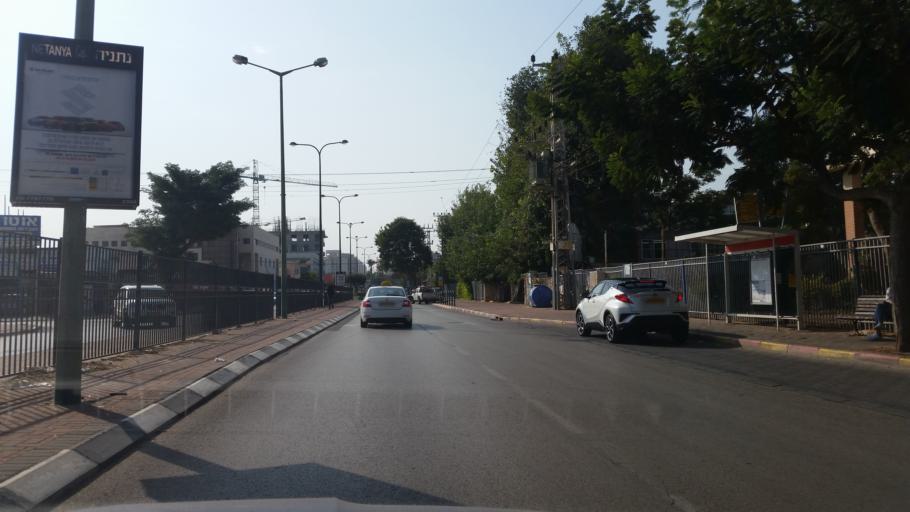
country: IL
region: Central District
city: Bet Yizhaq
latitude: 32.3166
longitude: 34.8738
